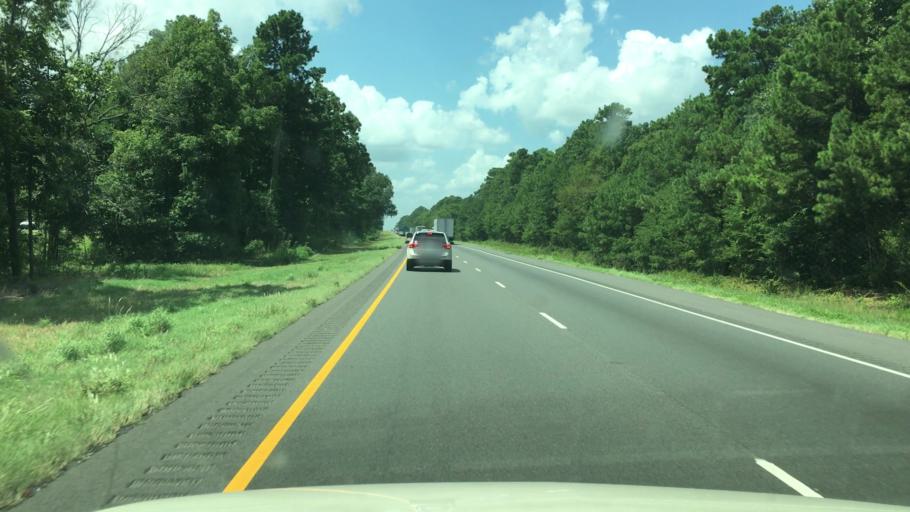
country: US
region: Arkansas
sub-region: Hempstead County
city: Hope
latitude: 33.7158
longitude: -93.5643
